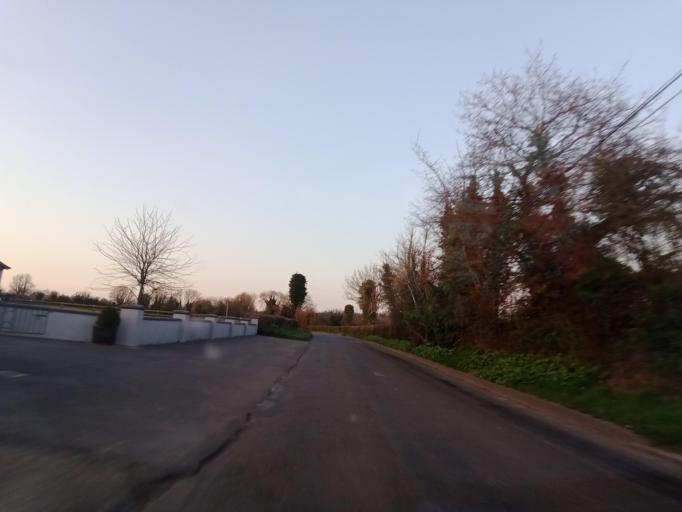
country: IE
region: Leinster
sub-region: Laois
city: Abbeyleix
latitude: 52.8824
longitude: -7.3092
